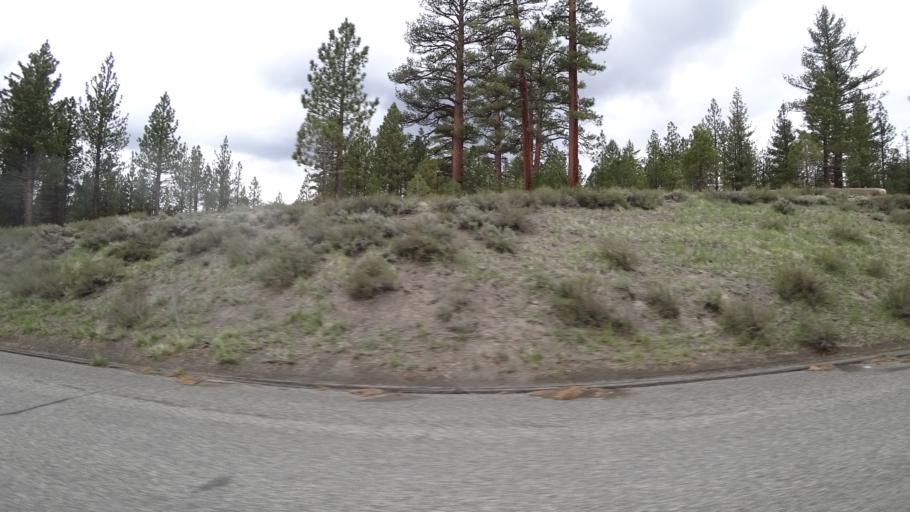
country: US
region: California
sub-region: Mono County
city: Mammoth Lakes
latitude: 37.7115
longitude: -118.9537
